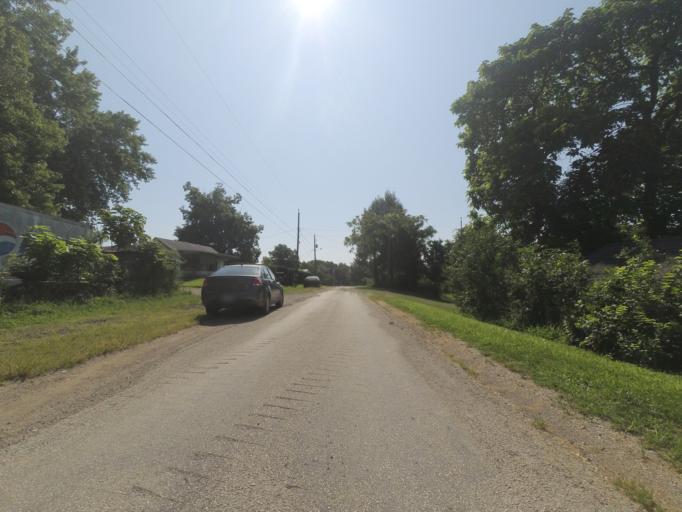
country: US
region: West Virginia
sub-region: Cabell County
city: Huntington
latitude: 38.4335
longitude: -82.4450
